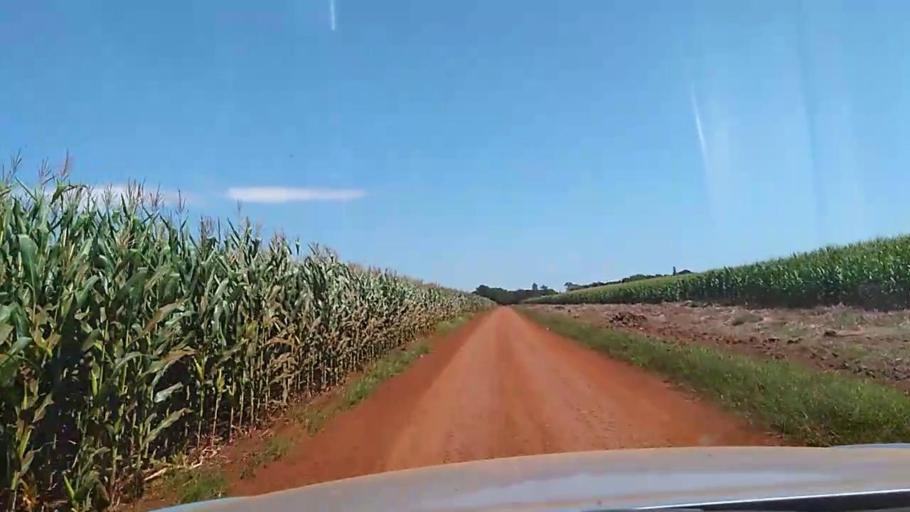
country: PY
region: Alto Parana
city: Naranjal
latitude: -25.9494
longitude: -55.1180
